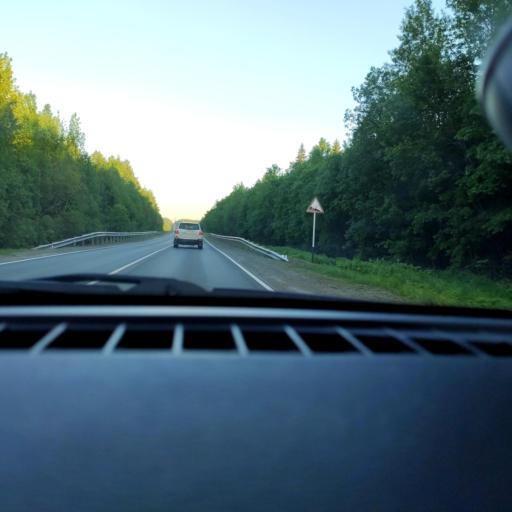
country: RU
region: Perm
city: Perm
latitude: 58.1707
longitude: 56.2349
